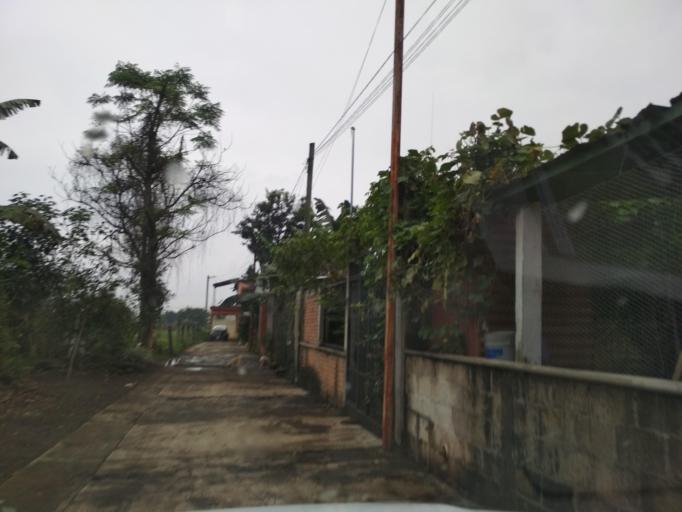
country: MX
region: Veracruz
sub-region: Cordoba
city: Veinte de Noviembre
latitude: 18.8676
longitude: -96.9560
